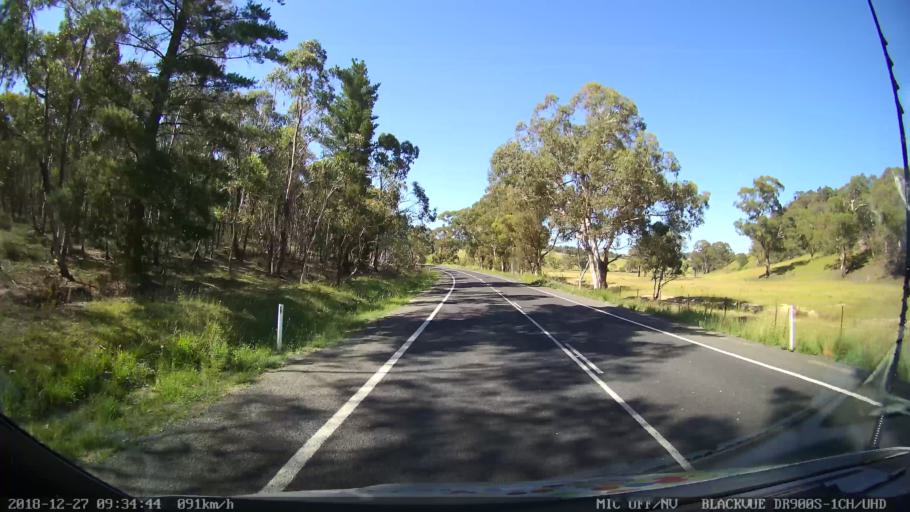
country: AU
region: New South Wales
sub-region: Lithgow
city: Portland
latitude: -33.2299
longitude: 150.0266
